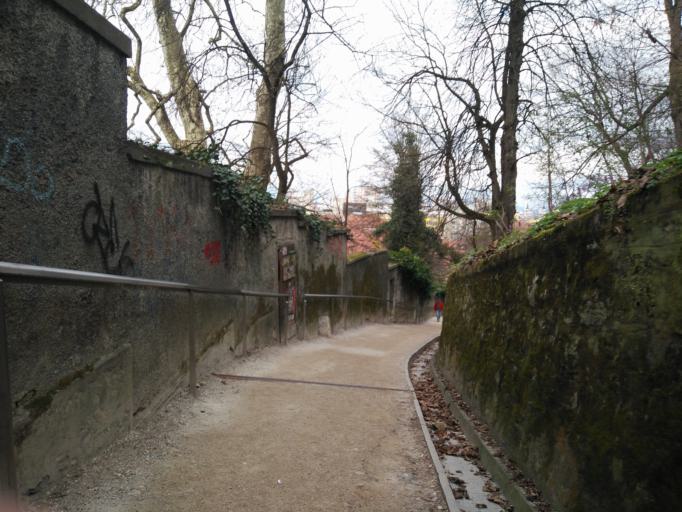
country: SI
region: Ljubljana
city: Ljubljana
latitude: 46.0499
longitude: 14.5080
